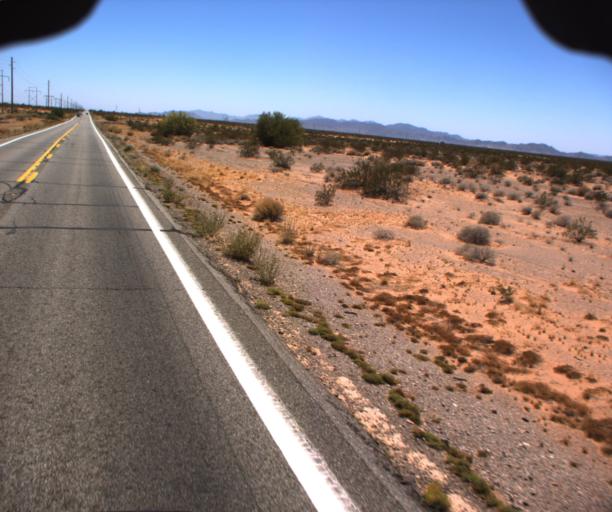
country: US
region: Arizona
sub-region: La Paz County
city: Quartzsite
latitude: 33.8614
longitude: -114.2170
